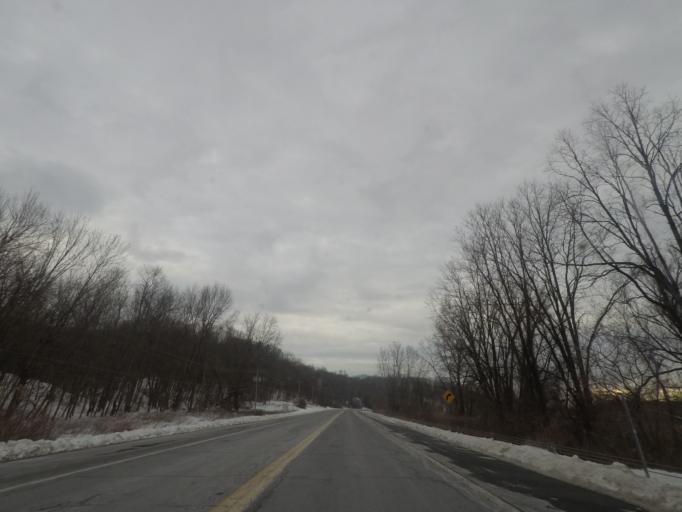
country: US
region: New York
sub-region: Rensselaer County
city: Castleton-on-Hudson
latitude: 42.5571
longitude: -73.7452
